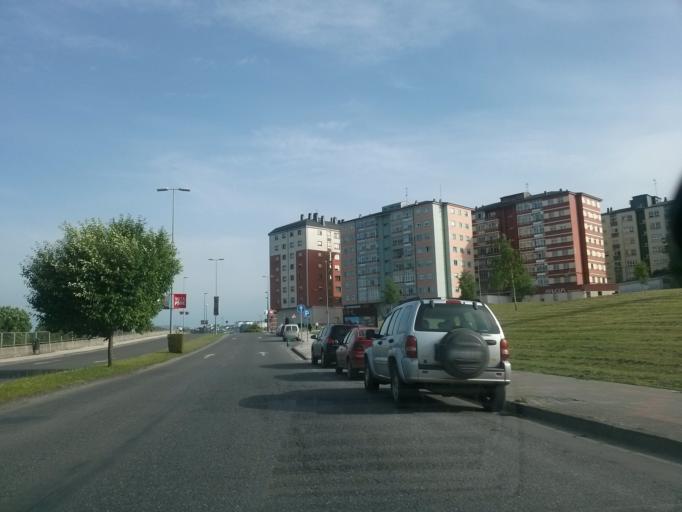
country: ES
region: Galicia
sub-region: Provincia de Lugo
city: Lugo
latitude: 43.0244
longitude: -7.5596
